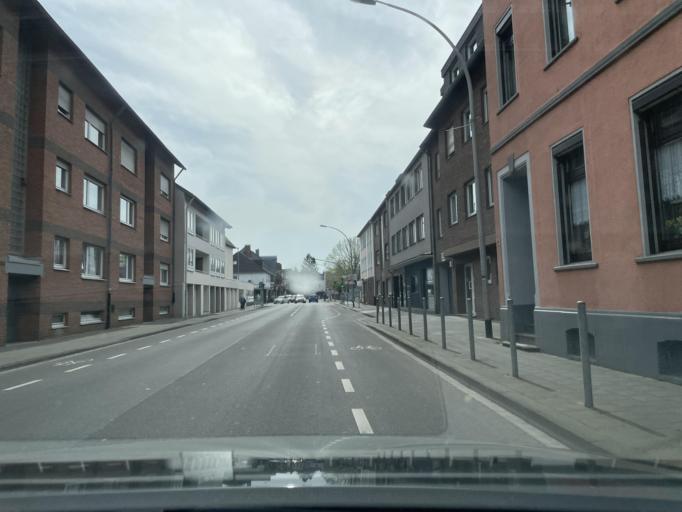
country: DE
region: North Rhine-Westphalia
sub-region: Regierungsbezirk Dusseldorf
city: Monchengladbach
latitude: 51.2056
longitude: 6.4109
